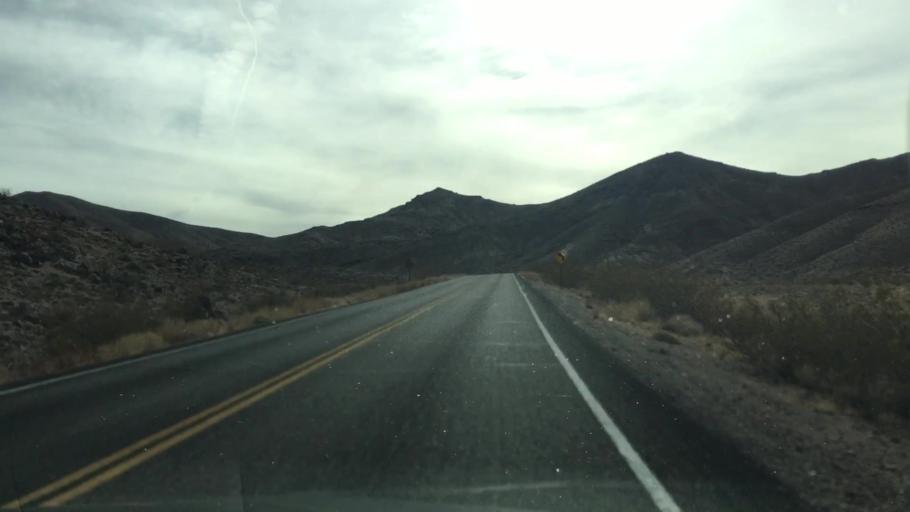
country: US
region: Nevada
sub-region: Nye County
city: Beatty
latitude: 36.7474
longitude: -116.9499
